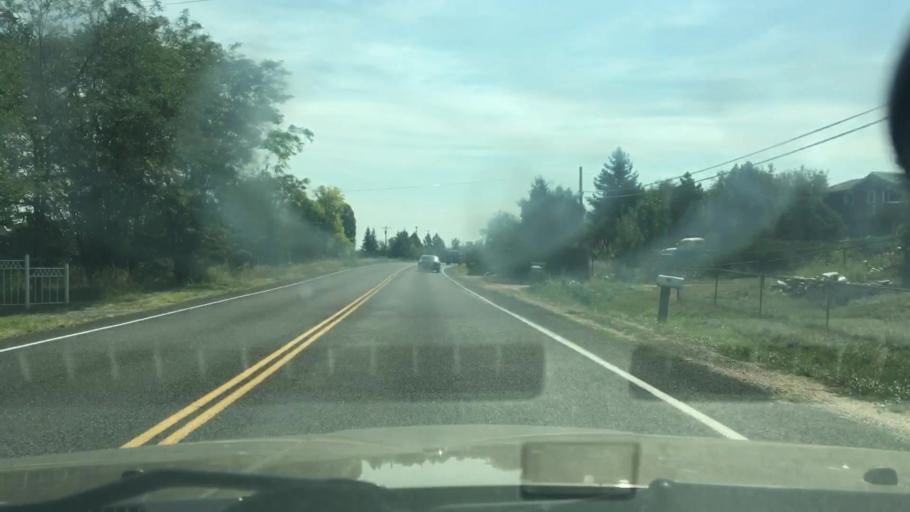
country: US
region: Colorado
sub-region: Larimer County
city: Loveland
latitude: 40.4344
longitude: -105.1964
